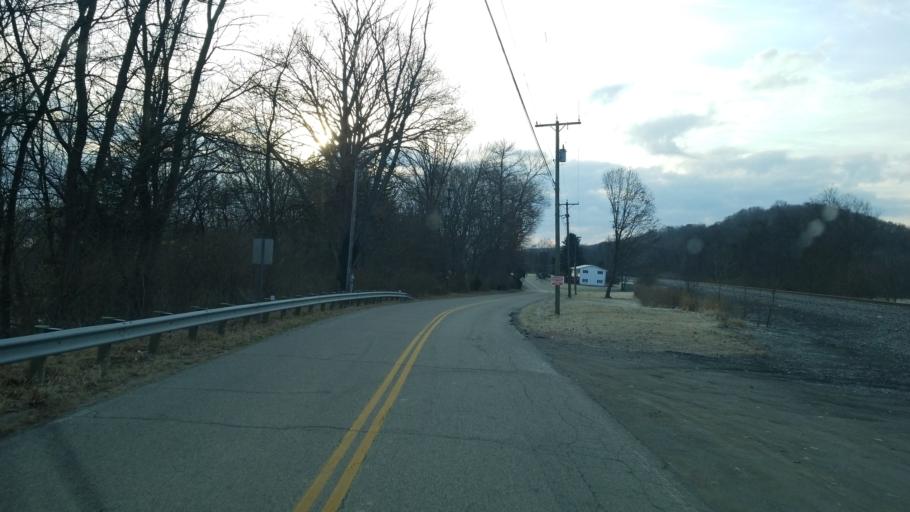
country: US
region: Ohio
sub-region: Ross County
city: Chillicothe
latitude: 39.2726
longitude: -82.9273
